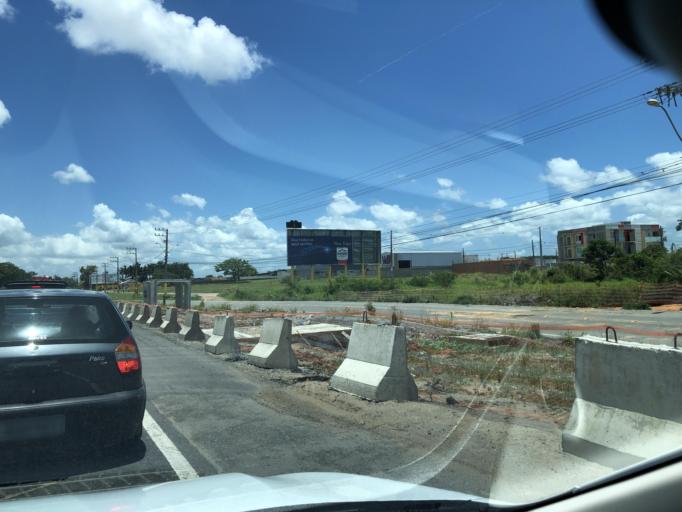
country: BR
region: Santa Catarina
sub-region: Joinville
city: Joinville
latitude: -26.4017
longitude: -48.7435
